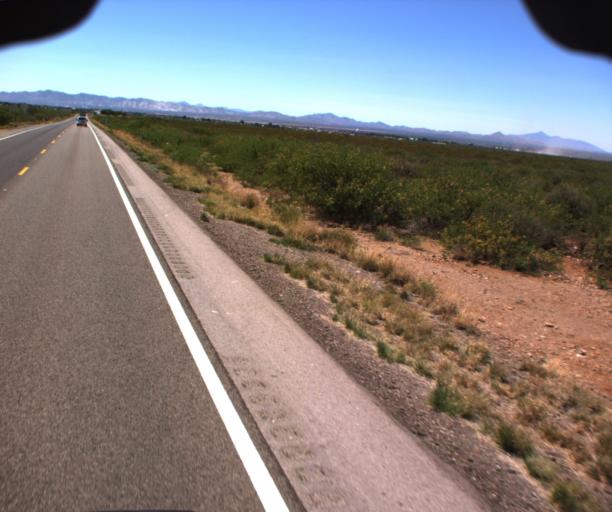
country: US
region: Arizona
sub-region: Cochise County
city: Douglas
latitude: 31.3904
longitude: -109.5118
